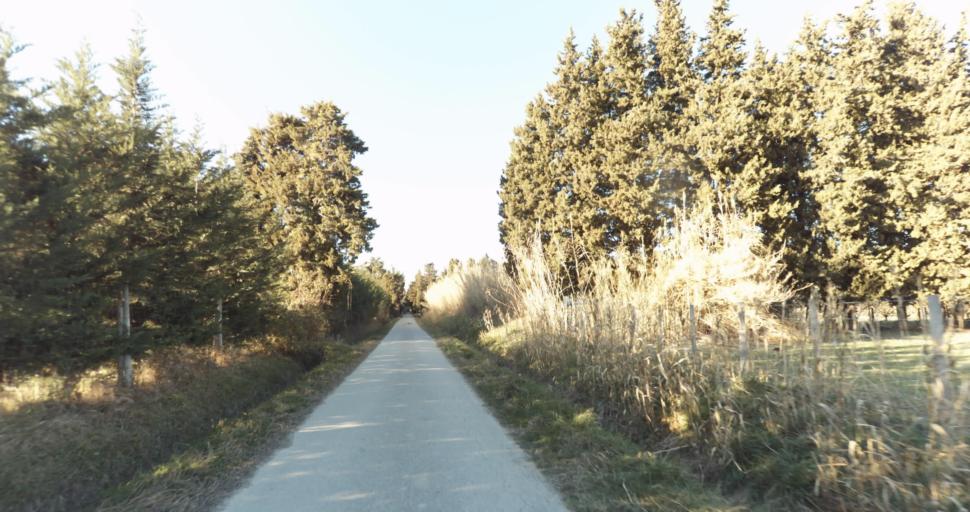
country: FR
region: Provence-Alpes-Cote d'Azur
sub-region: Departement des Bouches-du-Rhone
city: Barbentane
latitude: 43.9155
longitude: 4.7475
